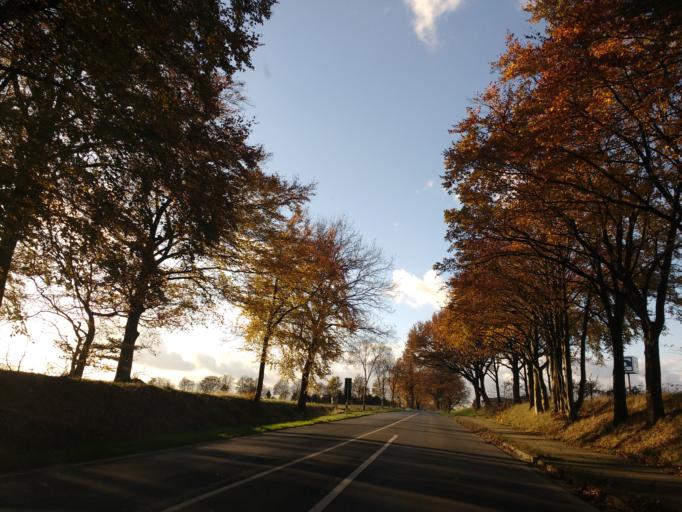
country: DE
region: Lower Saxony
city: Egestorf
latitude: 53.1936
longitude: 10.0803
